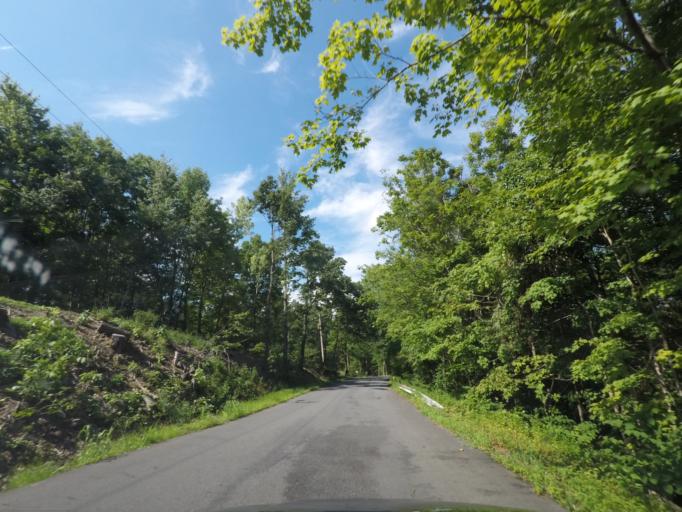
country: US
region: New York
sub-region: Rensselaer County
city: Averill Park
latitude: 42.6017
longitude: -73.5821
